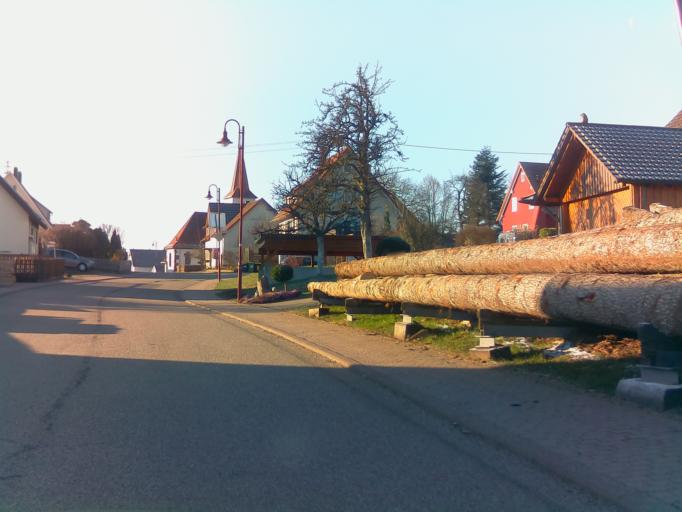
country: DE
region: Baden-Wuerttemberg
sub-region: Karlsruhe Region
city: Oberreichenbach
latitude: 48.7497
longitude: 8.6616
